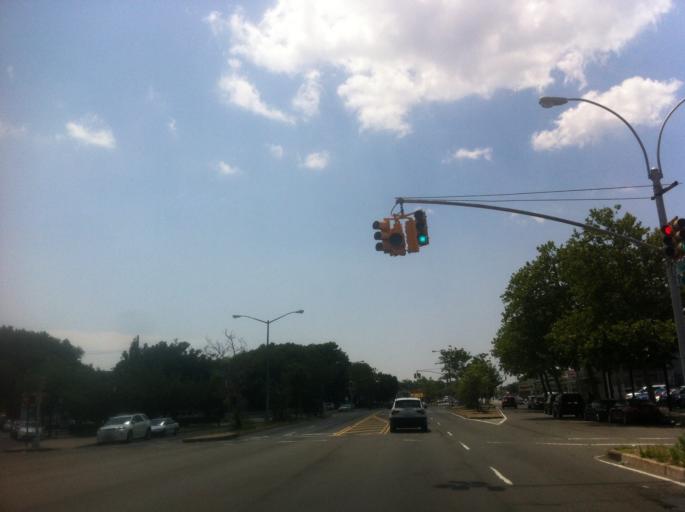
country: US
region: New York
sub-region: Kings County
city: Brooklyn
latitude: 40.6363
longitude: -73.9267
